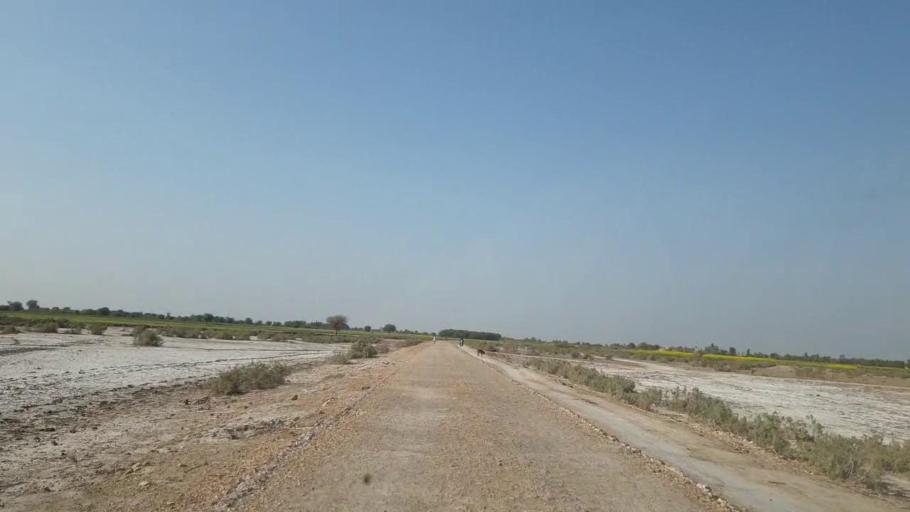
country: PK
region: Sindh
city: Tando Mittha Khan
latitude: 25.7582
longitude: 69.1948
